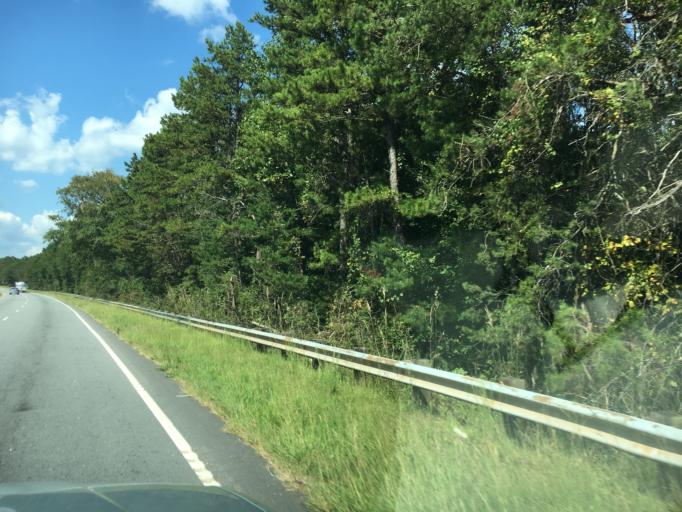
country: US
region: South Carolina
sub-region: Anderson County
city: Powdersville
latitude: 34.8041
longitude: -82.5116
